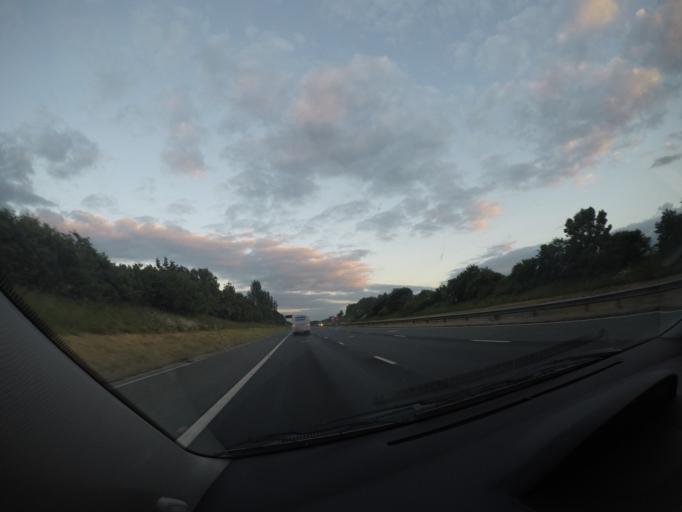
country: GB
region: England
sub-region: North Yorkshire
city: Boroughbridge
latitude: 54.0656
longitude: -1.3913
